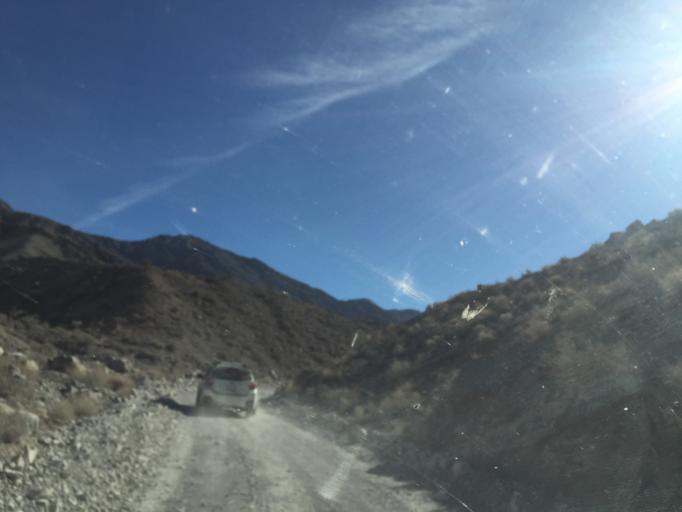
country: US
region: California
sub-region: Inyo County
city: Lone Pine
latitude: 36.8773
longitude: -117.5002
